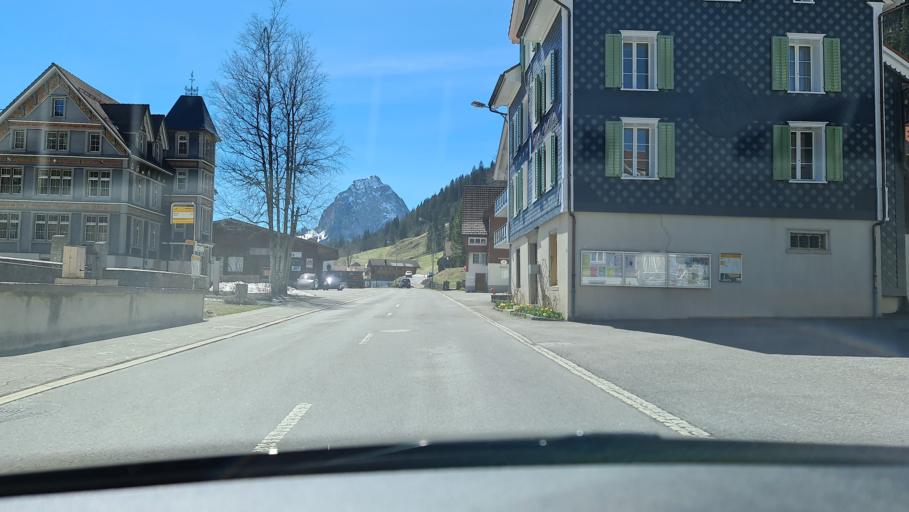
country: CH
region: Schwyz
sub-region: Bezirk Schwyz
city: Rothenthurm
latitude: 47.0710
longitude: 8.7159
